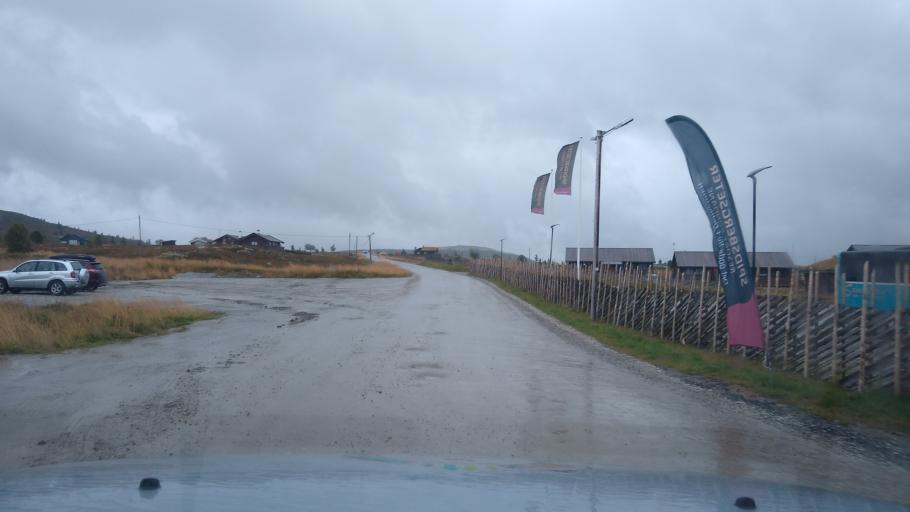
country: NO
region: Oppland
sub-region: Ringebu
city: Ringebu
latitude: 61.6720
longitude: 10.1036
